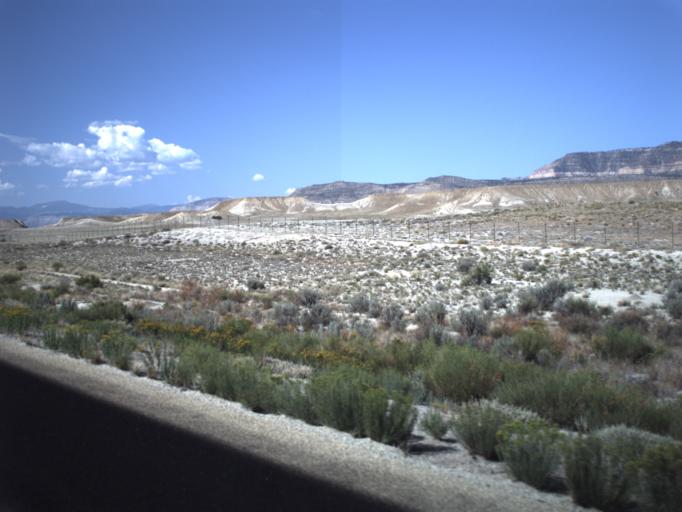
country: US
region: Utah
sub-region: Emery County
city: Ferron
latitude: 38.9769
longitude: -111.1764
